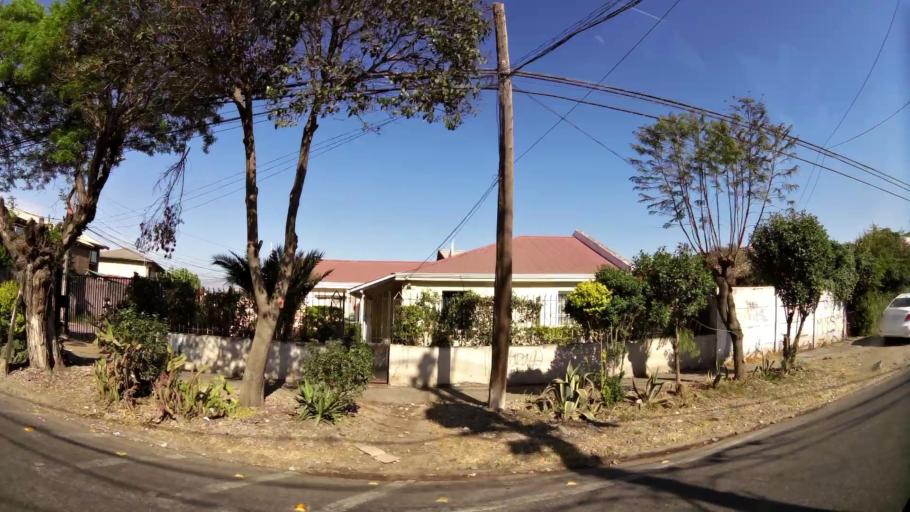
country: CL
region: Santiago Metropolitan
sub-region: Provincia de Maipo
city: San Bernardo
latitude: -33.6010
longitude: -70.7118
